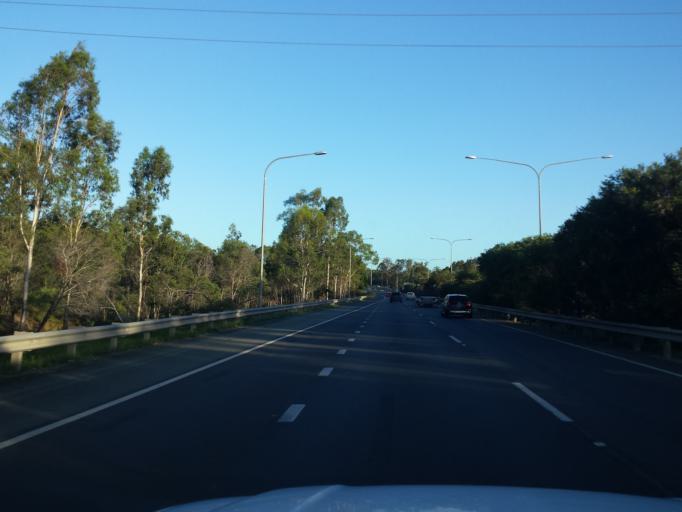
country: AU
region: Queensland
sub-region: Logan
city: Woodridge
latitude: -27.6545
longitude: 153.0742
